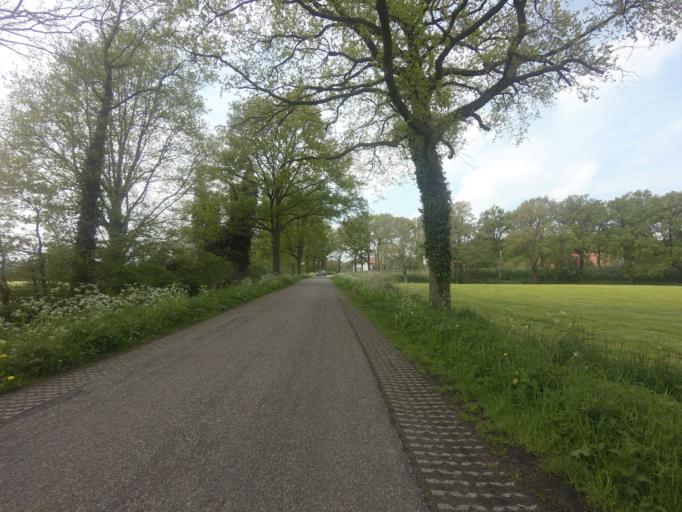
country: NL
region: Overijssel
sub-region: Gemeente Hof van Twente
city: Delden
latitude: 52.2451
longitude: 6.6794
